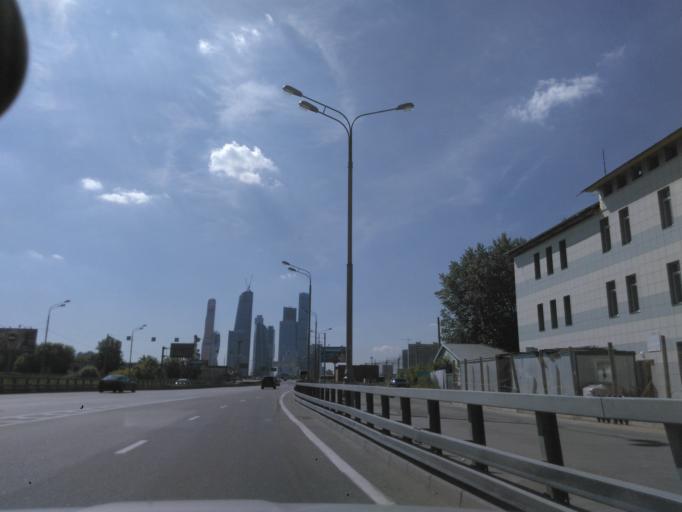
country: RU
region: Moscow
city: Sokol
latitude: 55.7667
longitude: 37.5181
